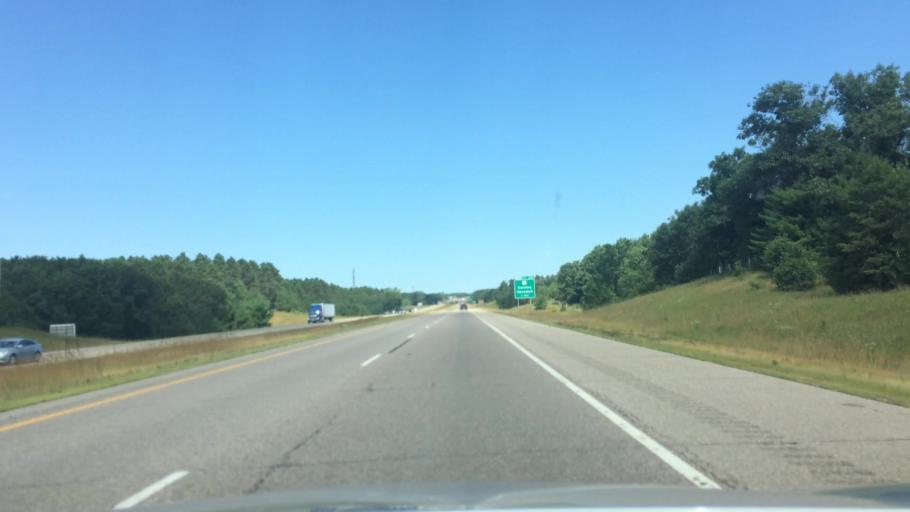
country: US
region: Wisconsin
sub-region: Marquette County
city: Westfield
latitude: 44.0174
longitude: -89.5122
